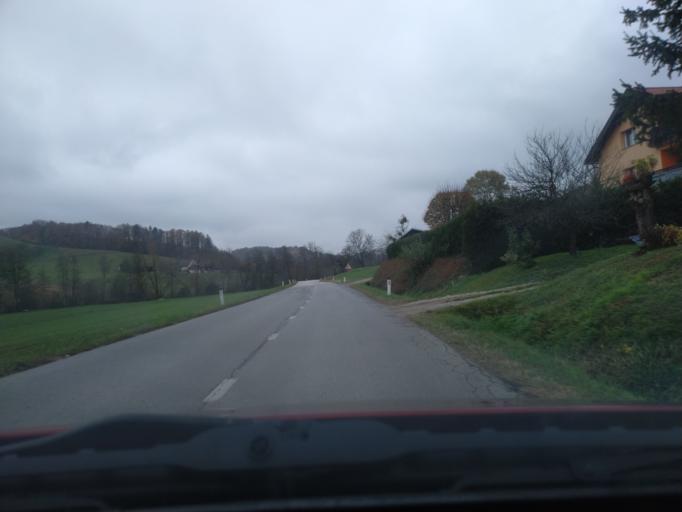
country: SI
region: Kungota
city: Zgornja Kungota
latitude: 46.6518
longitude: 15.6133
